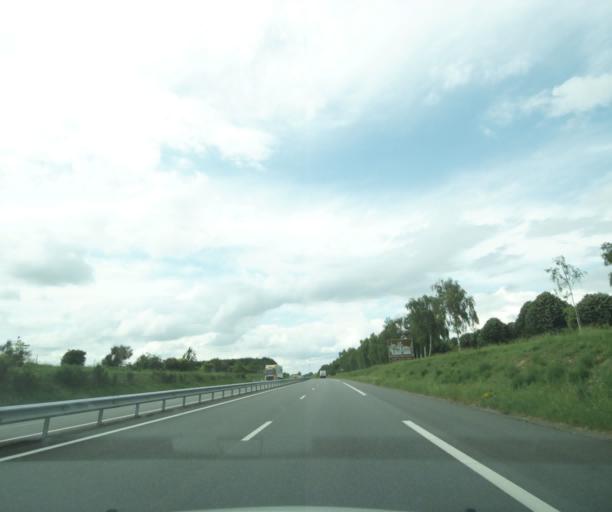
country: FR
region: Centre
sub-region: Departement du Cher
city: Trouy
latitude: 47.0248
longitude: 2.3795
